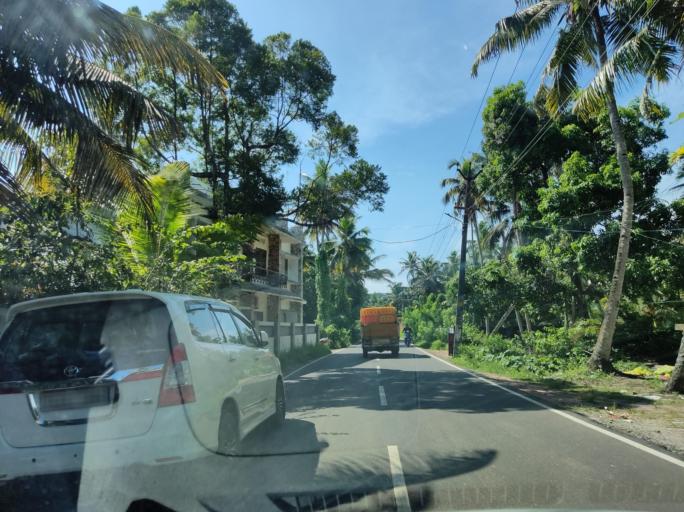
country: IN
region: Kerala
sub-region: Alappuzha
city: Kayankulam
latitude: 9.2797
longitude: 76.3995
